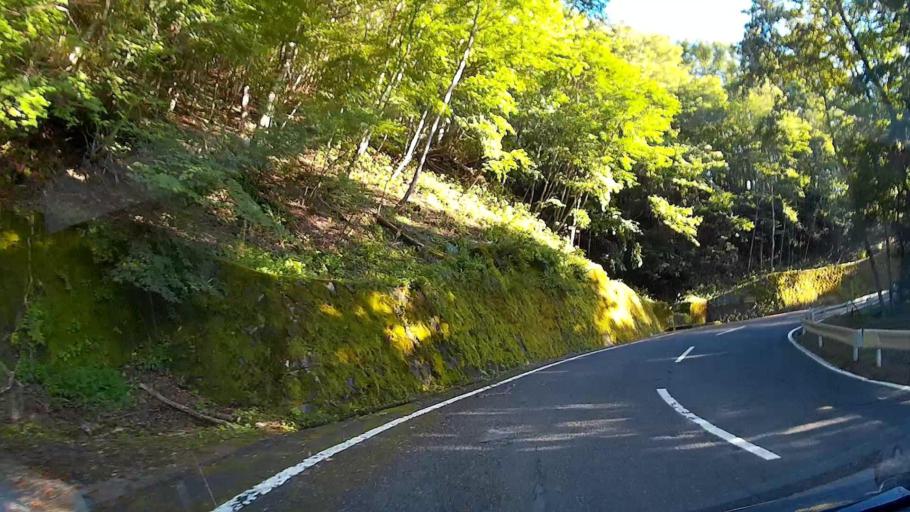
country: JP
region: Shizuoka
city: Shizuoka-shi
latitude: 35.1959
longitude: 138.2517
